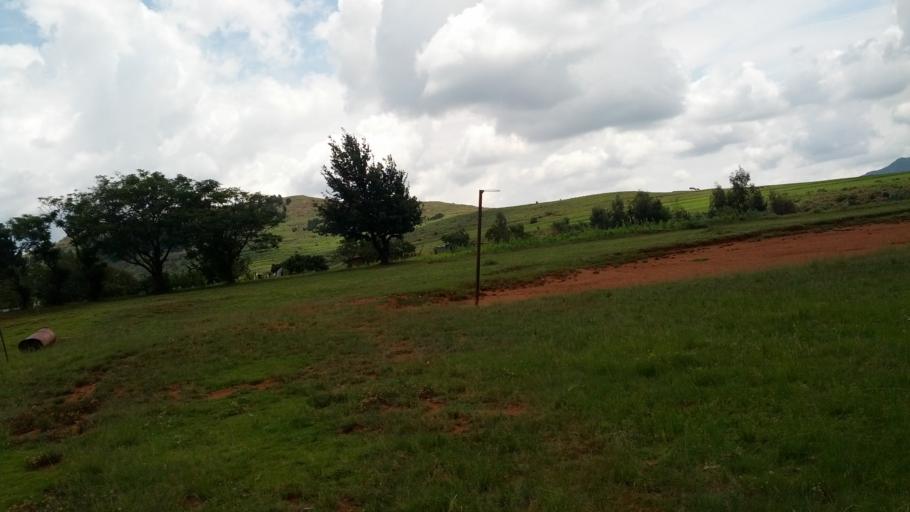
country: LS
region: Maseru
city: Nako
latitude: -29.5892
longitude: 27.7580
